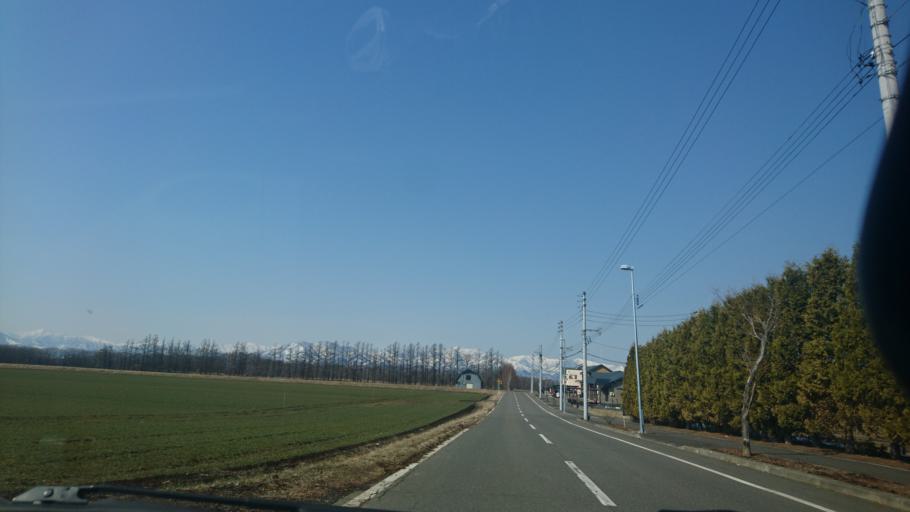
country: JP
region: Hokkaido
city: Obihiro
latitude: 42.9100
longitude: 143.0728
